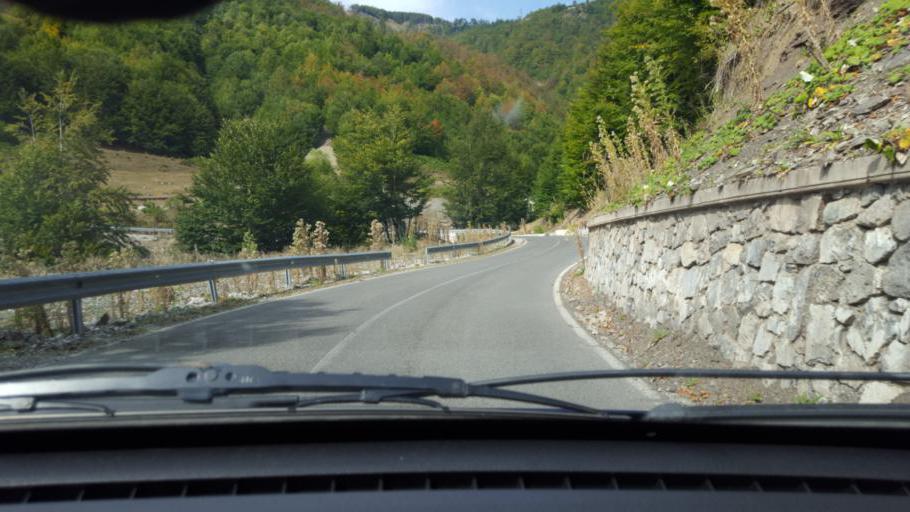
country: AL
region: Kukes
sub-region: Rrethi i Tropojes
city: Valbone
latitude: 42.5389
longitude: 19.6967
